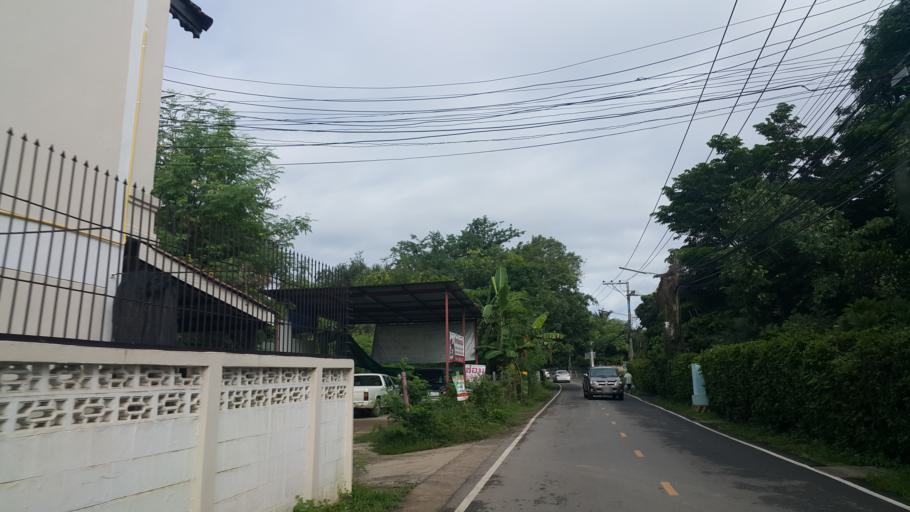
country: TH
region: Chiang Mai
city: Chiang Mai
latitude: 18.7481
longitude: 98.9689
